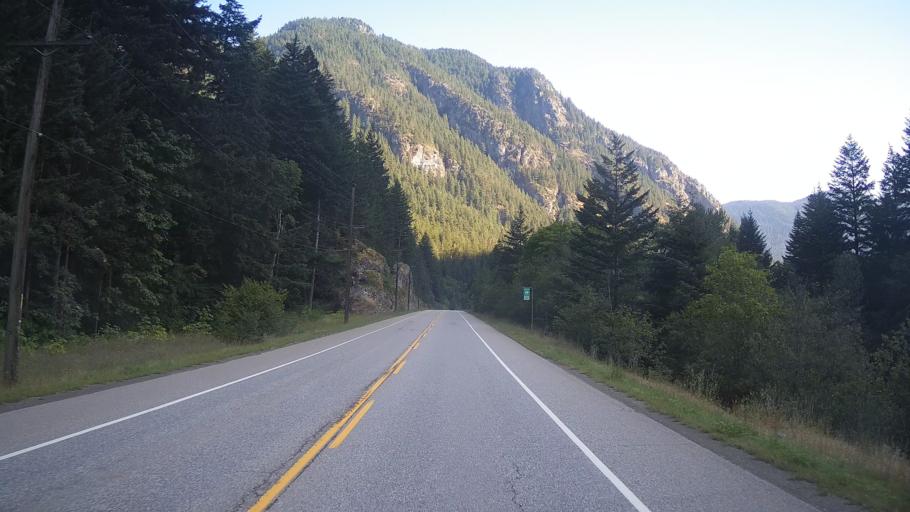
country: CA
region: British Columbia
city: Hope
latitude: 49.6042
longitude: -121.4156
